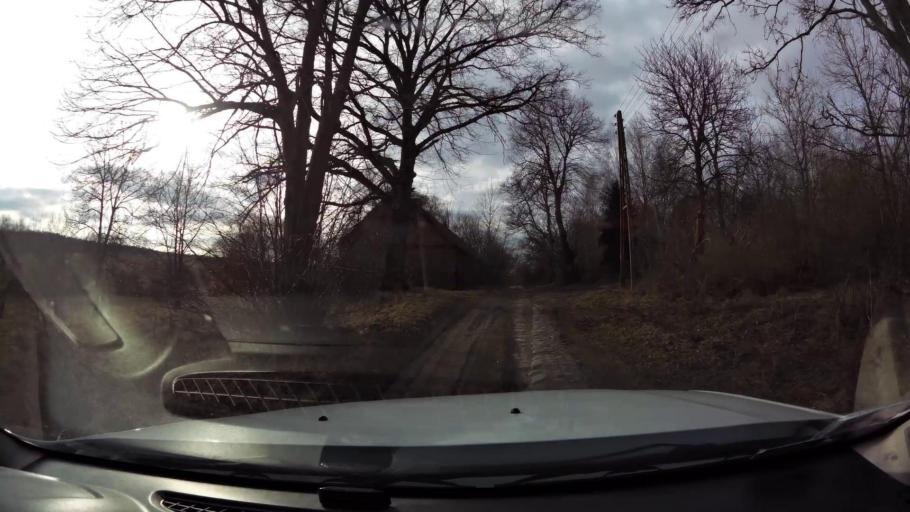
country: PL
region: West Pomeranian Voivodeship
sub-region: Powiat drawski
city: Drawsko Pomorskie
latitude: 53.5209
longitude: 15.7062
